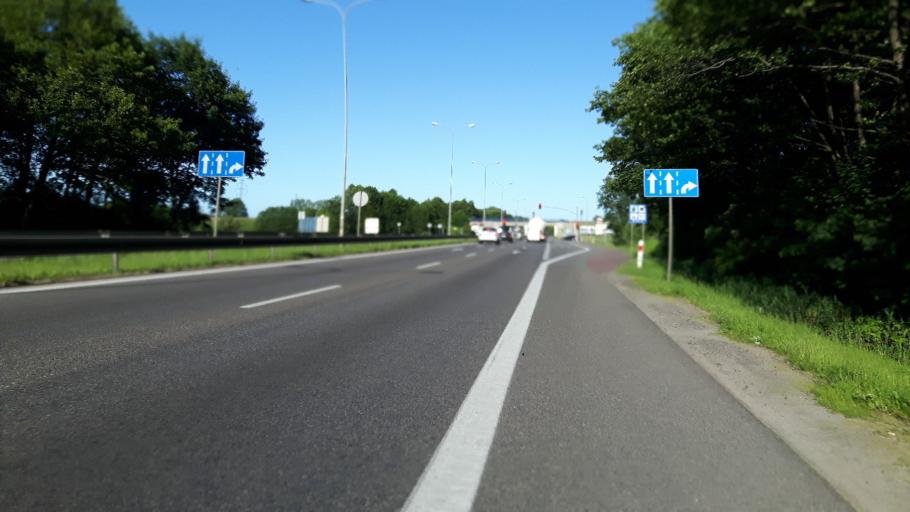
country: PL
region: Pomeranian Voivodeship
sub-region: Powiat wejherowski
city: Reda
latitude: 54.6048
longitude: 18.3361
